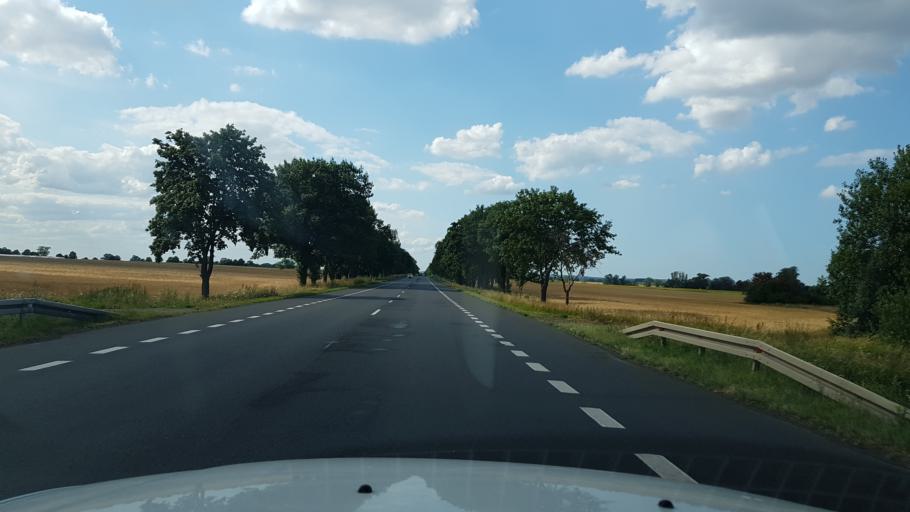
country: PL
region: West Pomeranian Voivodeship
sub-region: Powiat gryfinski
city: Stare Czarnowo
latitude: 53.2048
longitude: 14.8149
